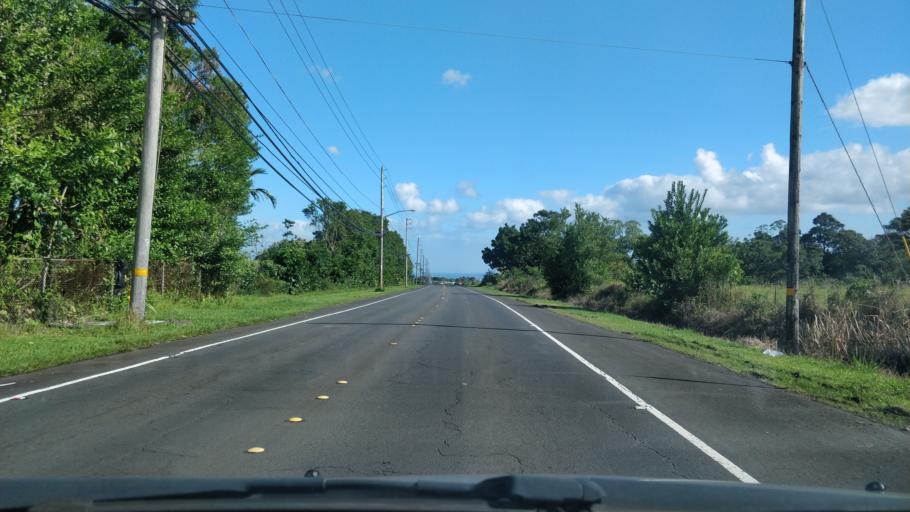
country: US
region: Hawaii
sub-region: Hawaii County
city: Hilo
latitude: 19.6698
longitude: -155.0944
